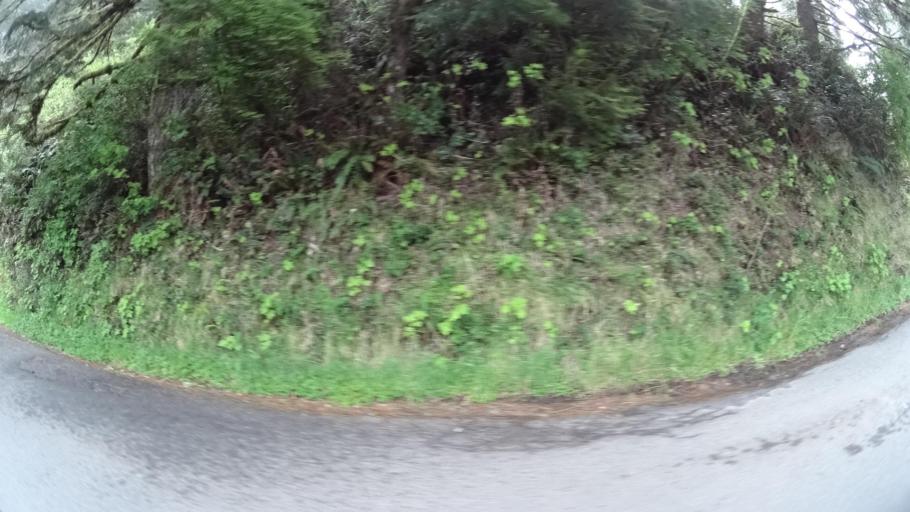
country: US
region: California
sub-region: Humboldt County
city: Ferndale
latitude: 40.5168
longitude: -124.2703
